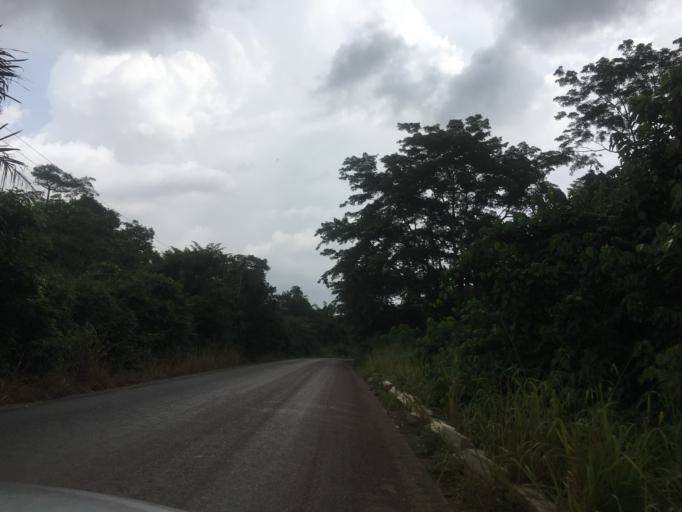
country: GH
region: Ashanti
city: Mamponteng
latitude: 6.6827
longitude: -1.5619
